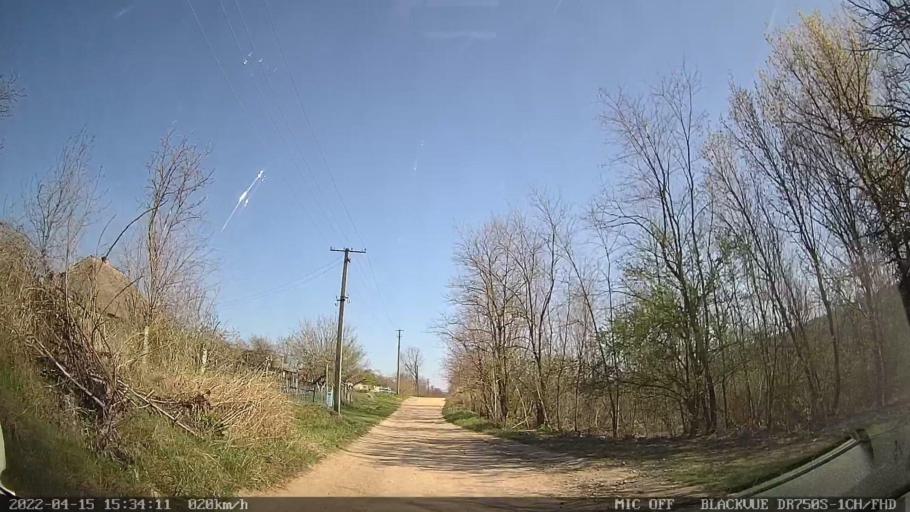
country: MD
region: Raionul Ocnita
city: Otaci
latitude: 48.3480
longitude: 27.9262
